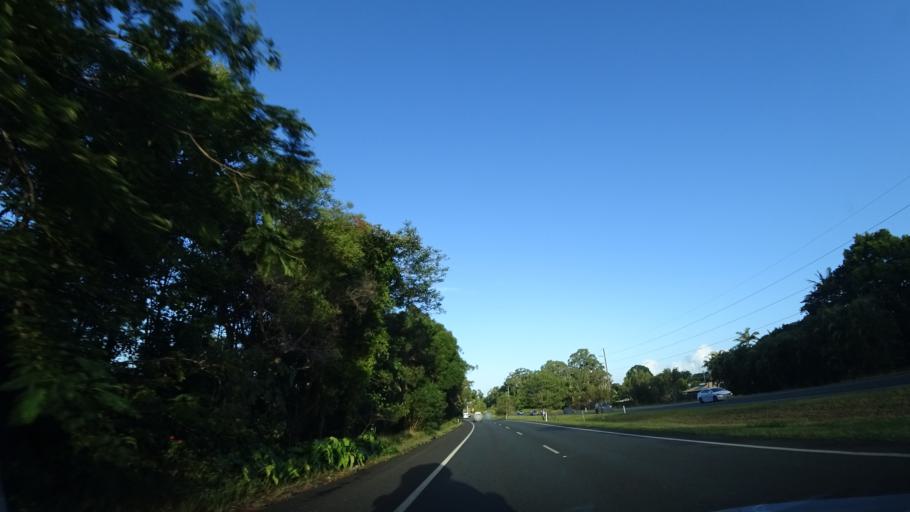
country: AU
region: Queensland
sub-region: Sunshine Coast
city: Buderim
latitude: -26.6630
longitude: 153.0588
